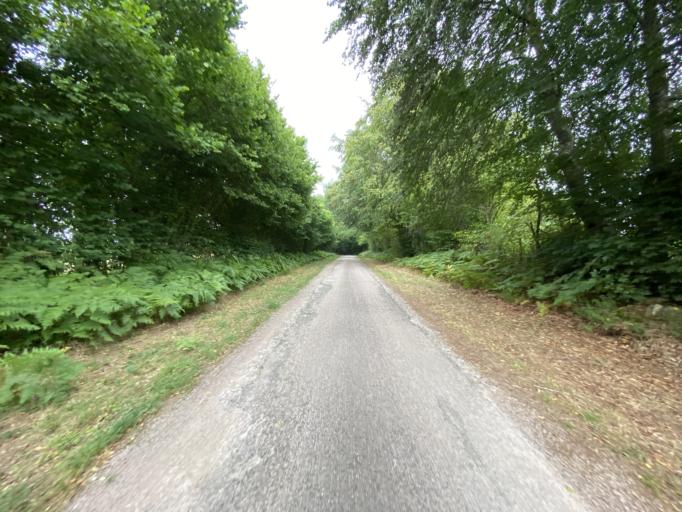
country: FR
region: Bourgogne
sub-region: Departement de la Cote-d'Or
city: Saulieu
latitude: 47.2630
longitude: 4.1416
